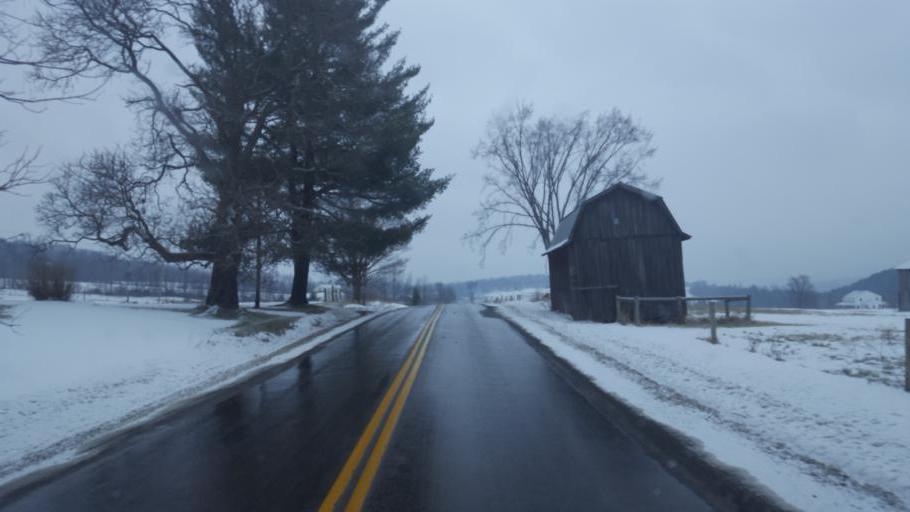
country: US
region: Pennsylvania
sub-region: Tioga County
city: Elkland
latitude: 42.0810
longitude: -77.4518
